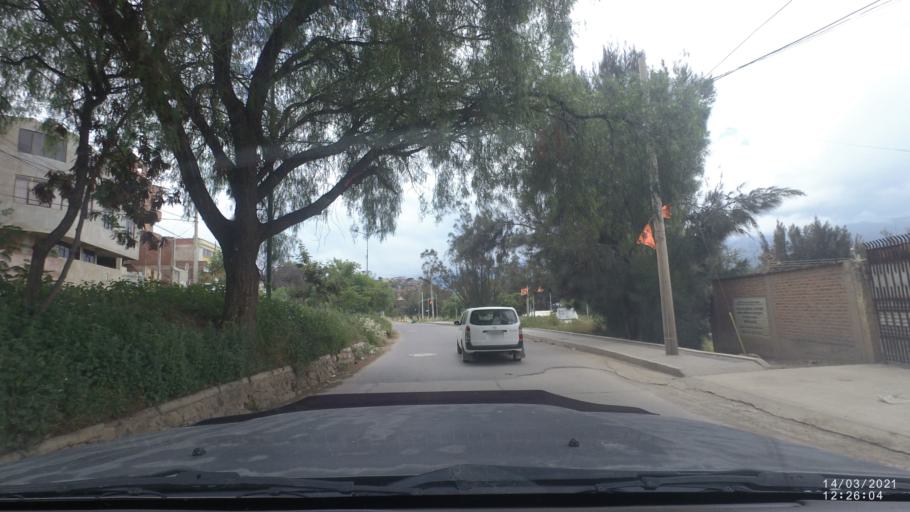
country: BO
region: Cochabamba
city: Cochabamba
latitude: -17.4170
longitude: -66.1405
